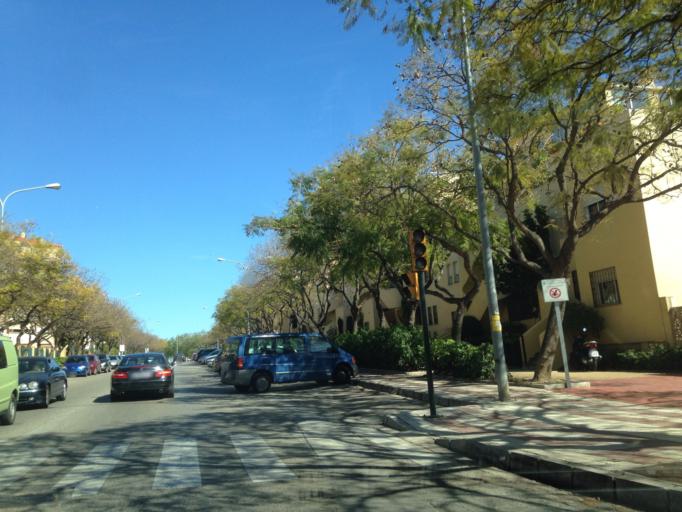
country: ES
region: Andalusia
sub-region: Provincia de Malaga
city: Benalmadena
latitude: 36.5942
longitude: -4.5359
